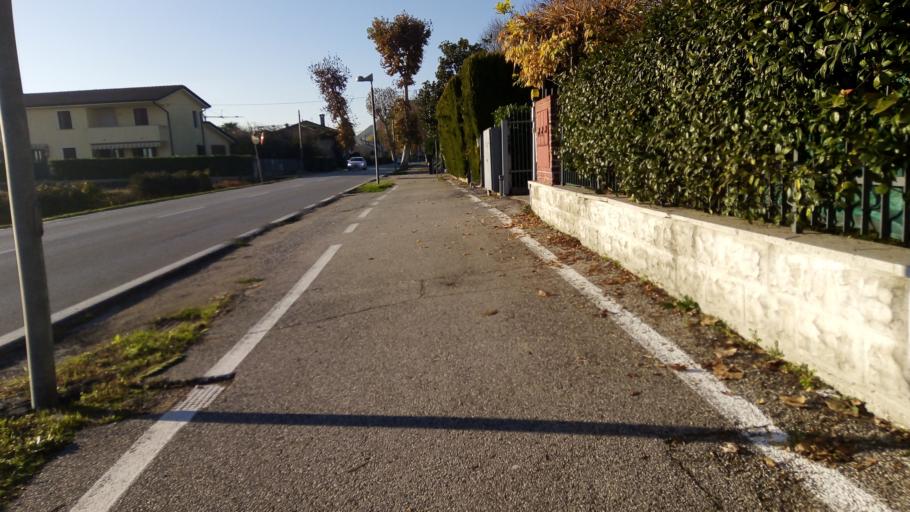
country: IT
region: Veneto
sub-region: Provincia di Padova
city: Abano Terme
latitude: 45.3636
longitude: 11.7754
